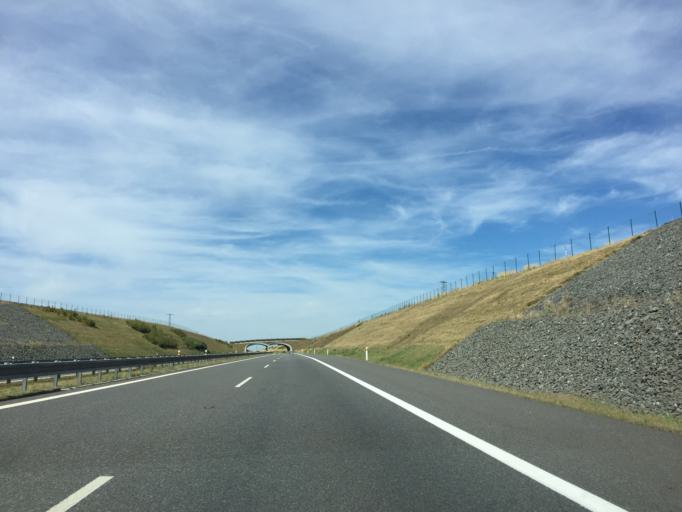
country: CZ
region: Jihocesky
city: Sobeslav
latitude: 49.3027
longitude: 14.7377
